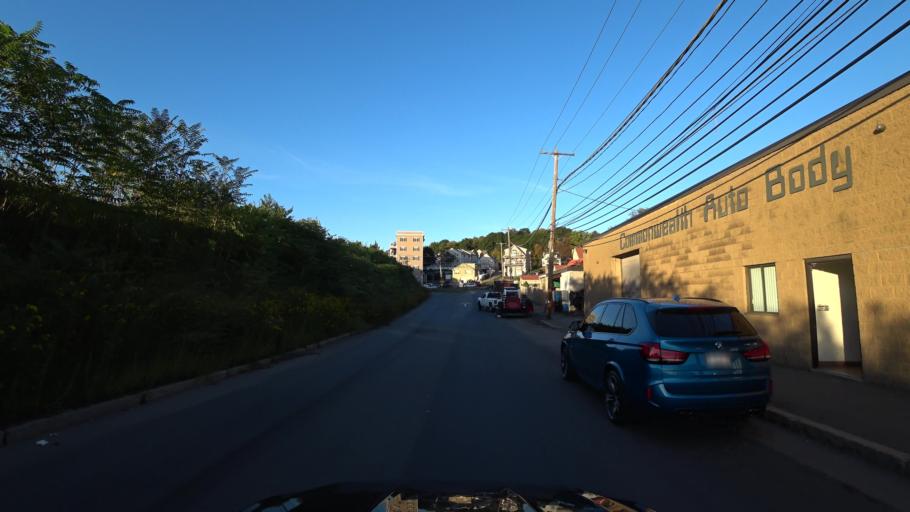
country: US
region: Massachusetts
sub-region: Suffolk County
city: Revere
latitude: 42.4032
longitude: -71.0034
